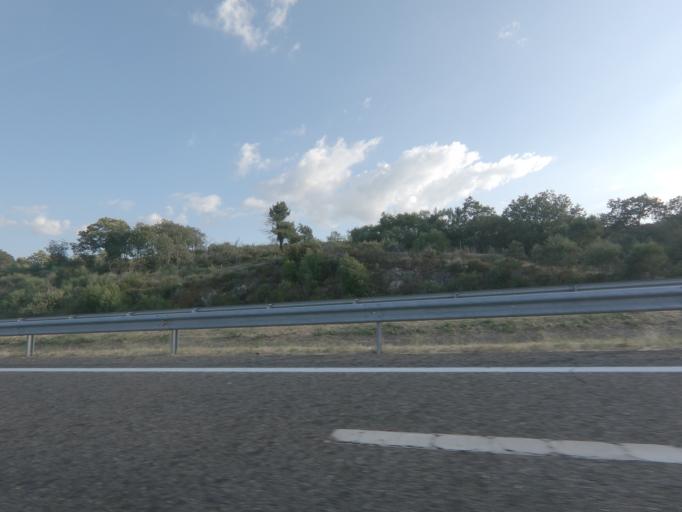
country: ES
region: Galicia
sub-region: Provincia de Ourense
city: Cualedro
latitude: 41.9788
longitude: -7.5368
